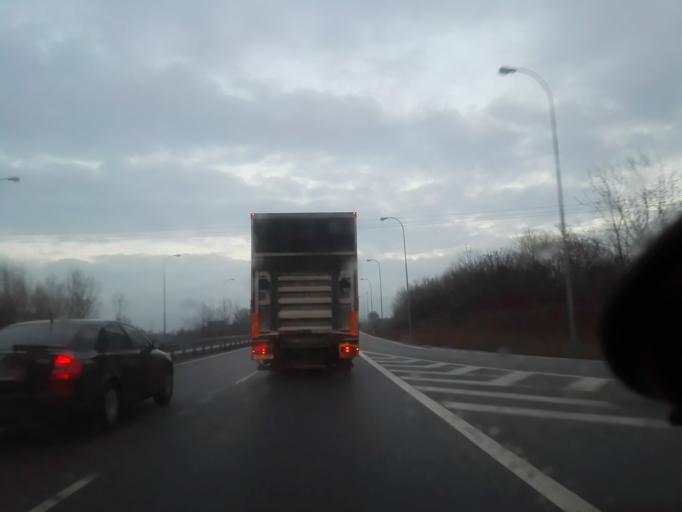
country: PL
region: Masovian Voivodeship
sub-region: Powiat wolominski
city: Radzymin
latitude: 52.3991
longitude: 21.1748
